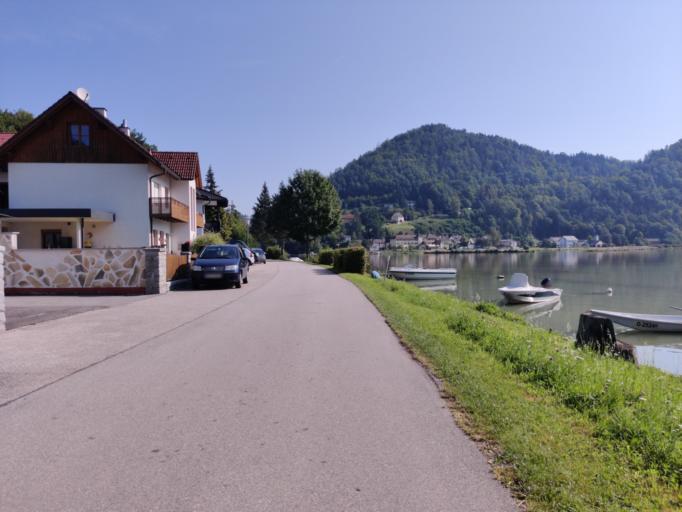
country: AT
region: Upper Austria
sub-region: Politischer Bezirk Rohrbach
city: Kleinzell im Muehlkreis
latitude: 48.4217
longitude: 13.9773
